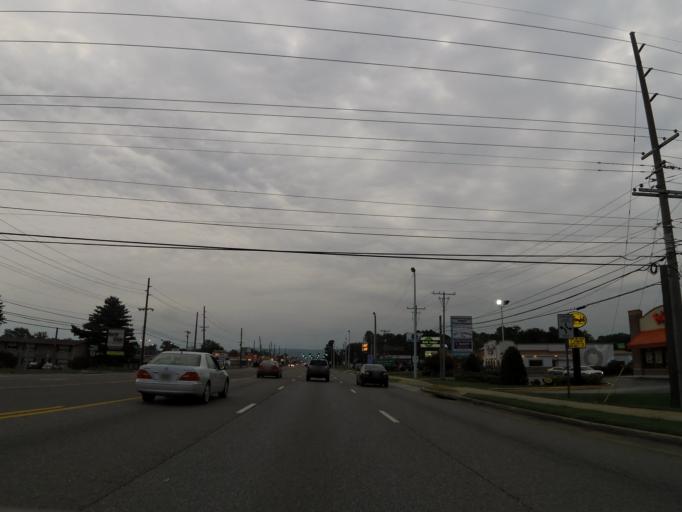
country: US
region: Alabama
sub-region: Madison County
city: Huntsville
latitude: 34.7349
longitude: -86.6362
